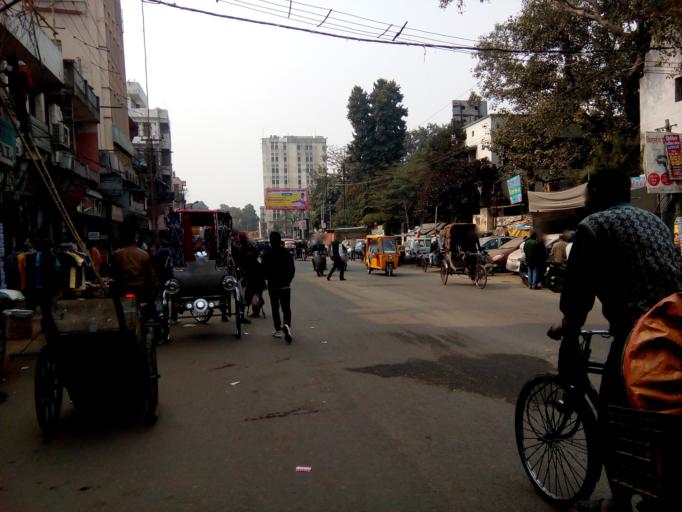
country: IN
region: Bihar
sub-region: Patna
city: Patna
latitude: 25.6197
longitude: 85.1575
